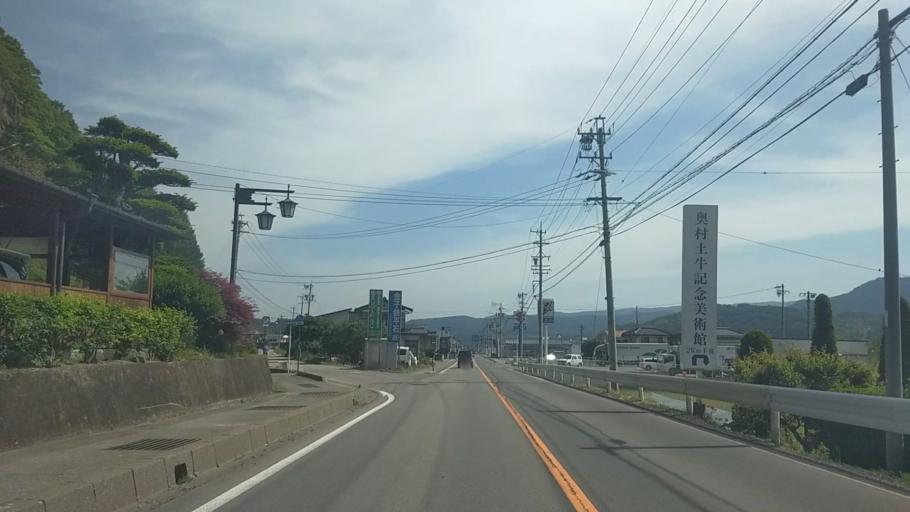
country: JP
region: Nagano
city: Saku
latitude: 36.1549
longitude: 138.4774
